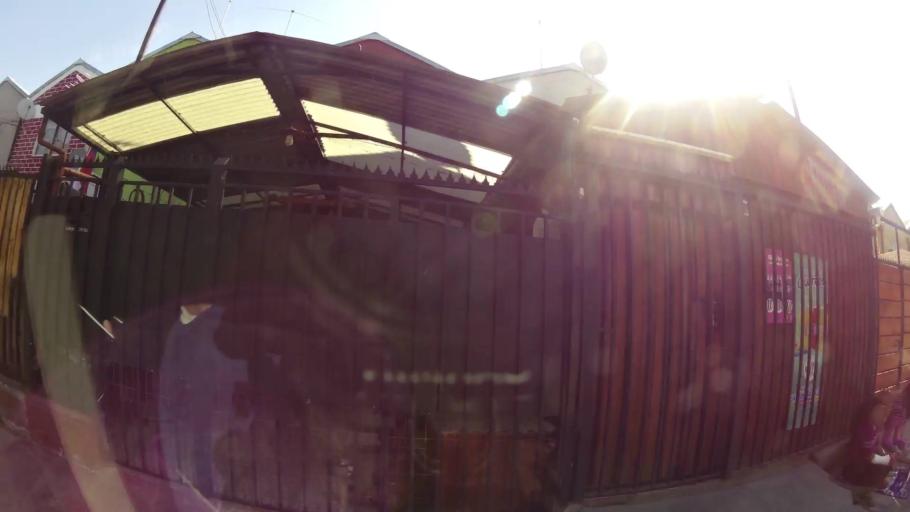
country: CL
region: Santiago Metropolitan
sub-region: Provincia de Santiago
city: La Pintana
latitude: -33.5630
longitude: -70.6221
